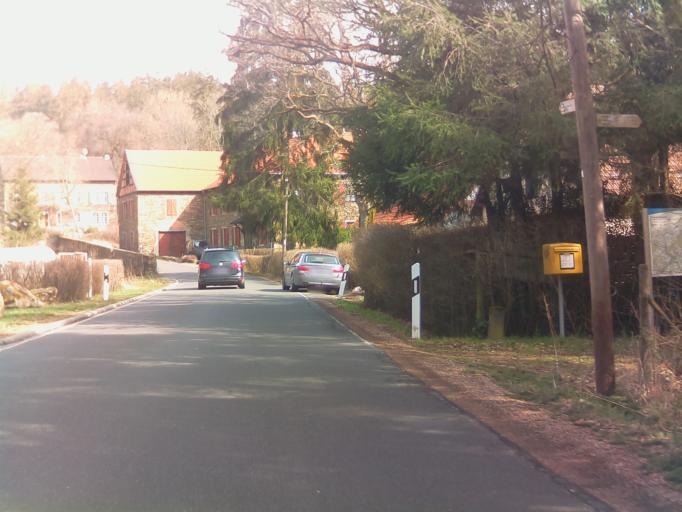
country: DE
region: Rheinland-Pfalz
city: Munchwald
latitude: 49.9138
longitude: 7.6675
